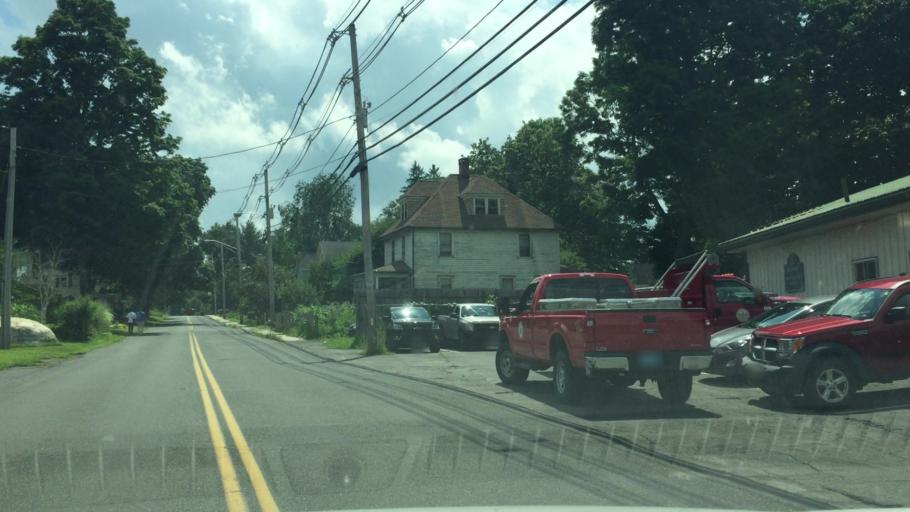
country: US
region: Massachusetts
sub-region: Berkshire County
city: Great Barrington
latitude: 42.2005
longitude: -73.3570
